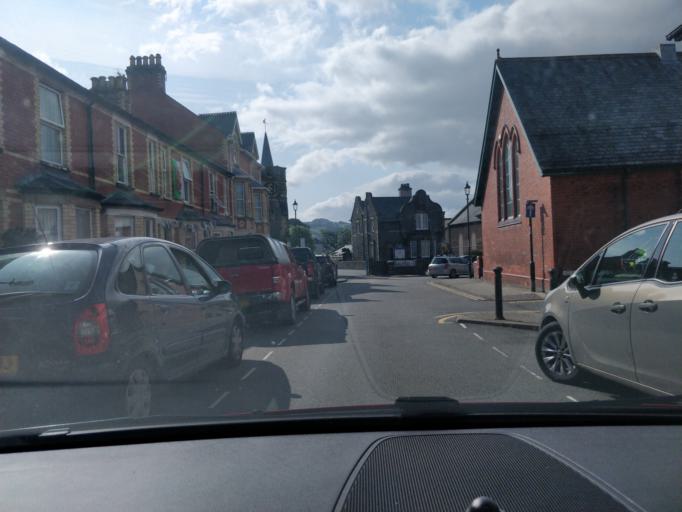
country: GB
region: Wales
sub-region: Conwy
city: Llanrwst
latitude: 53.1378
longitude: -3.7960
